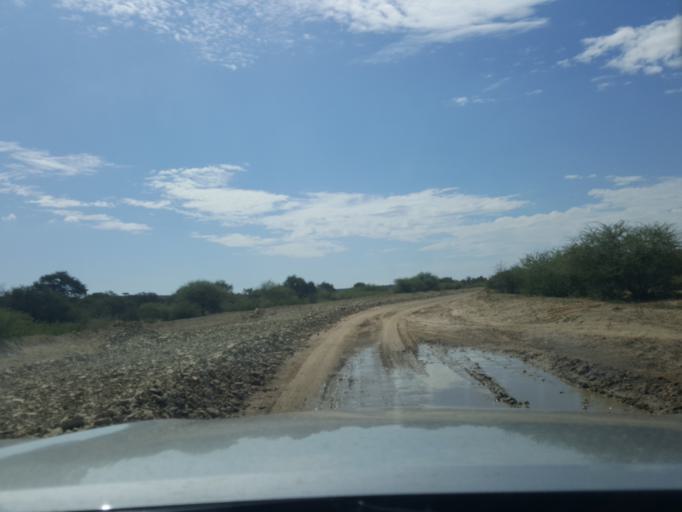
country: BW
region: Kweneng
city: Letlhakeng
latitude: -23.9858
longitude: 24.9688
